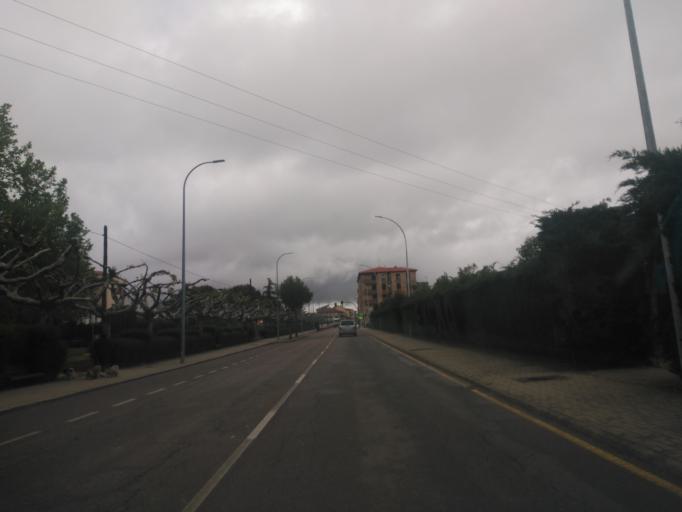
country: ES
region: Castille and Leon
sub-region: Provincia de Salamanca
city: Guijuelo
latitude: 40.5514
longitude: -5.6751
